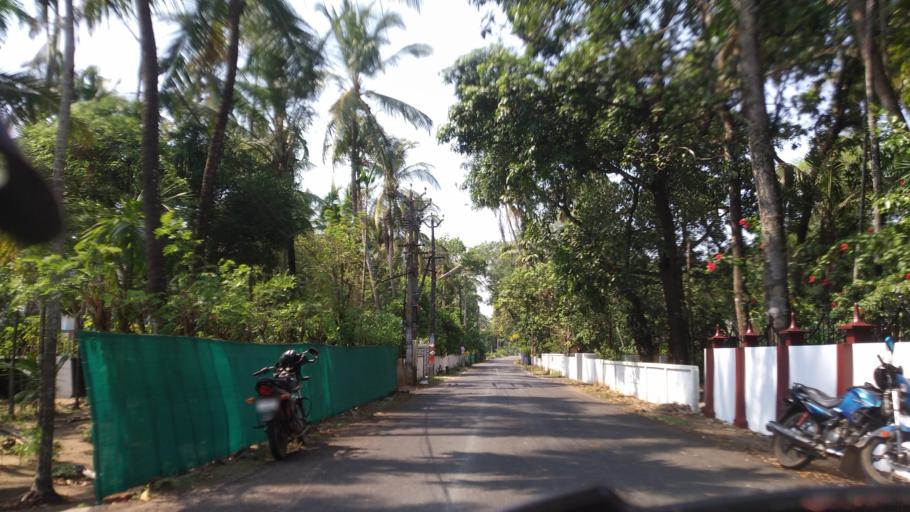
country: IN
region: Kerala
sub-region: Thrissur District
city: Thanniyam
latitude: 10.3651
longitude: 76.1071
